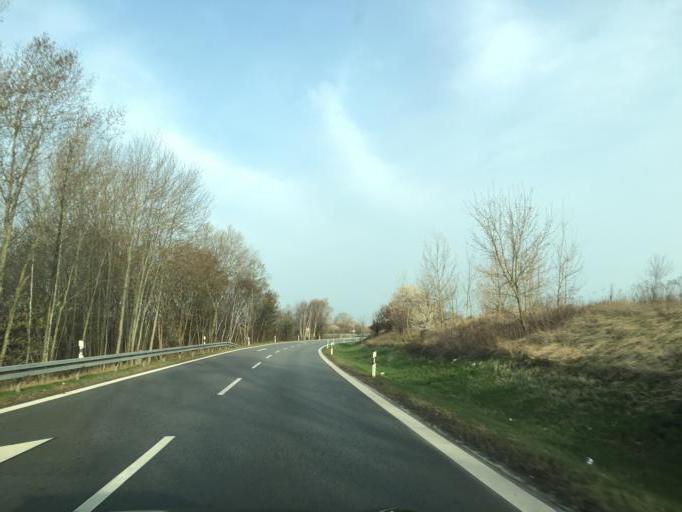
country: DE
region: Berlin
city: Blankenfelde
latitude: 52.6489
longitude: 13.4220
